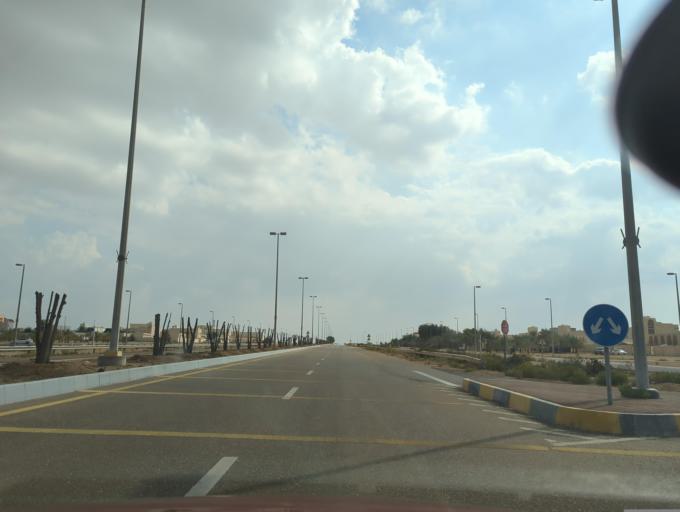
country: AE
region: Abu Dhabi
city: Abu Dhabi
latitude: 24.3720
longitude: 54.7170
